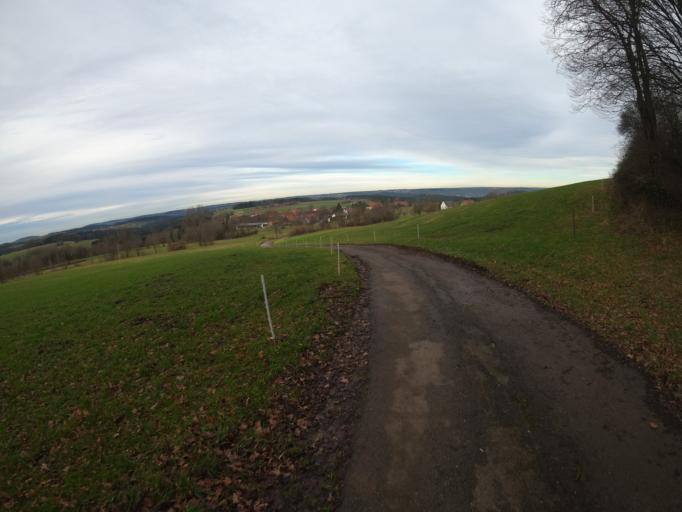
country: DE
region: Baden-Wuerttemberg
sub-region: Regierungsbezirk Stuttgart
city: Ottenbach
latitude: 48.7587
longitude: 9.7580
